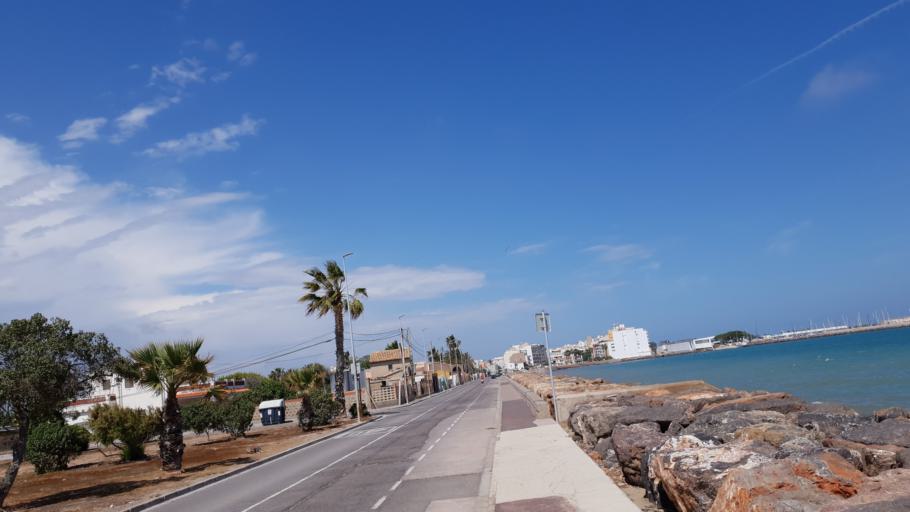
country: ES
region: Valencia
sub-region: Provincia de Castello
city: Burriana
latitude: 39.8594
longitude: -0.0828
